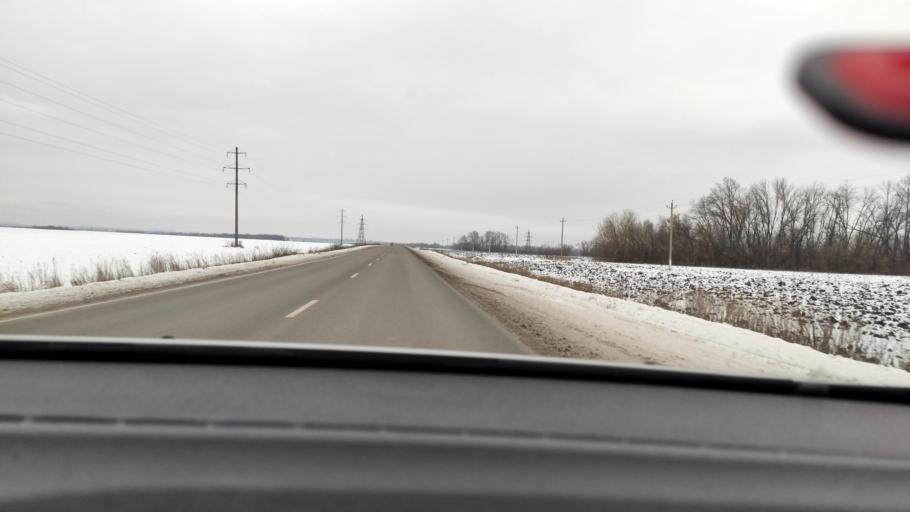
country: RU
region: Voronezj
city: Latnaya
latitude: 51.7456
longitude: 38.9349
